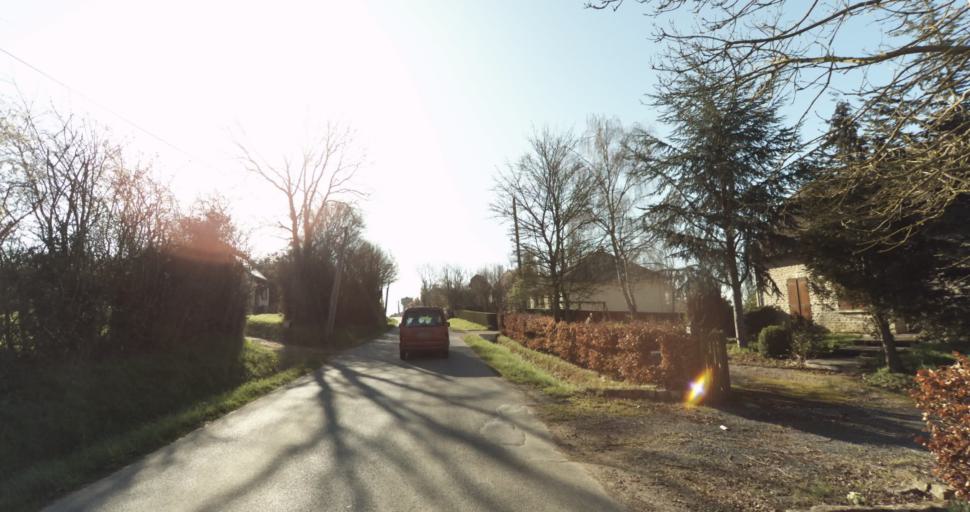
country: FR
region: Lower Normandy
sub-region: Departement du Calvados
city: Saint-Pierre-sur-Dives
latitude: 49.0078
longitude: -0.0154
